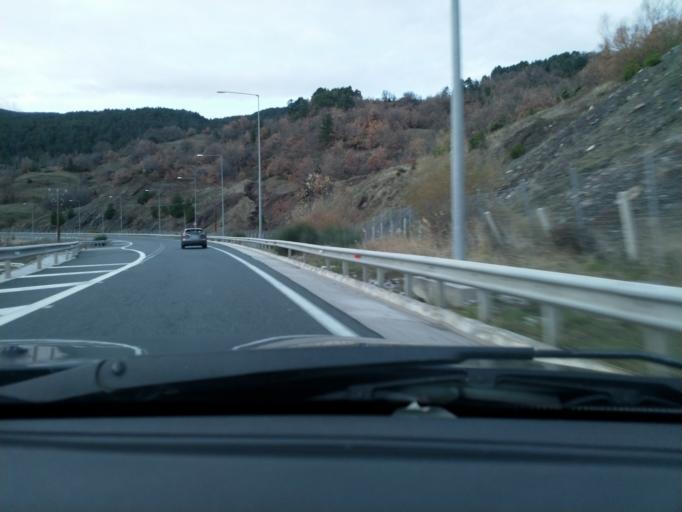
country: GR
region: Epirus
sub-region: Nomos Ioanninon
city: Metsovo
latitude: 39.7931
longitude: 21.3063
